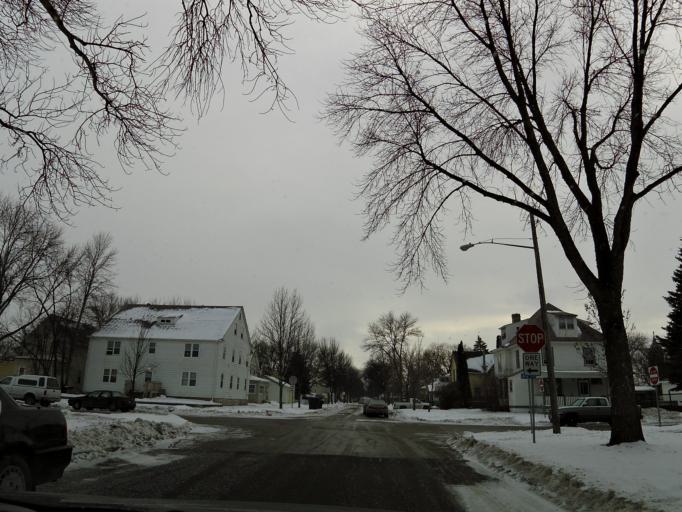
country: US
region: North Dakota
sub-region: Grand Forks County
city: Grand Forks
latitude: 47.9274
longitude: -97.0361
